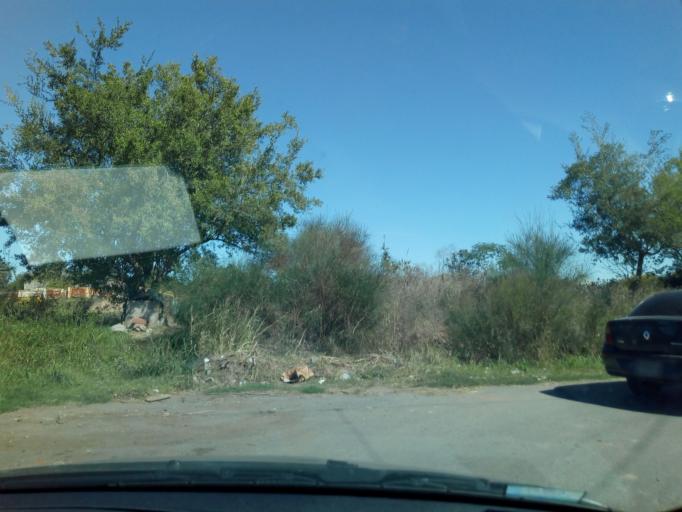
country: AR
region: Buenos Aires
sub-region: Partido de La Plata
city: La Plata
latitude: -35.0014
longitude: -58.0467
